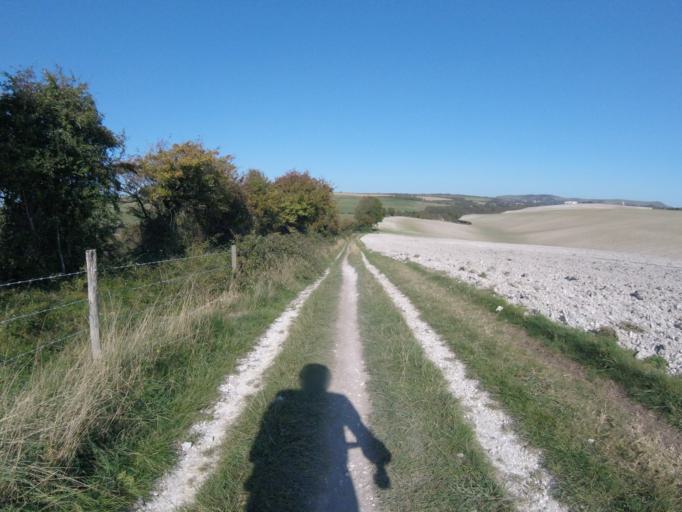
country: GB
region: England
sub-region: Brighton and Hove
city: Rottingdean
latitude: 50.8608
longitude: -0.0510
